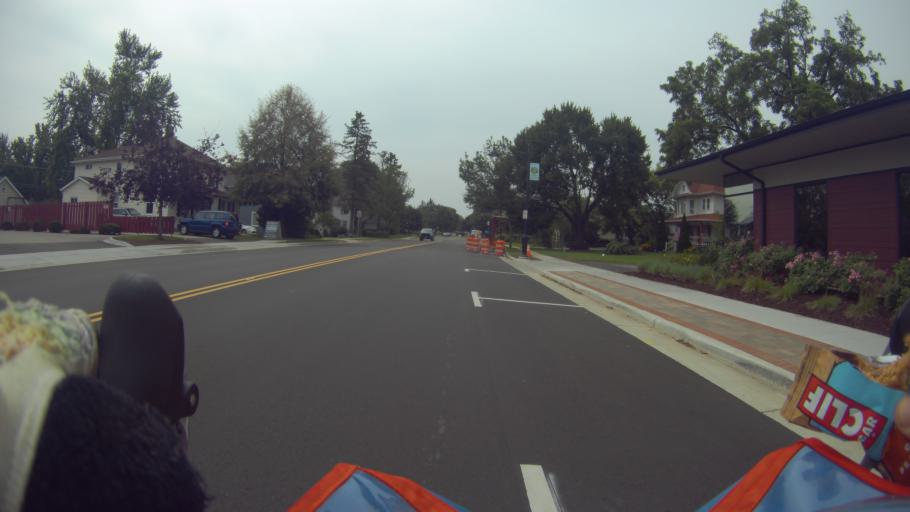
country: US
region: Wisconsin
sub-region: Dane County
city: Verona
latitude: 42.9869
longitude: -89.5334
